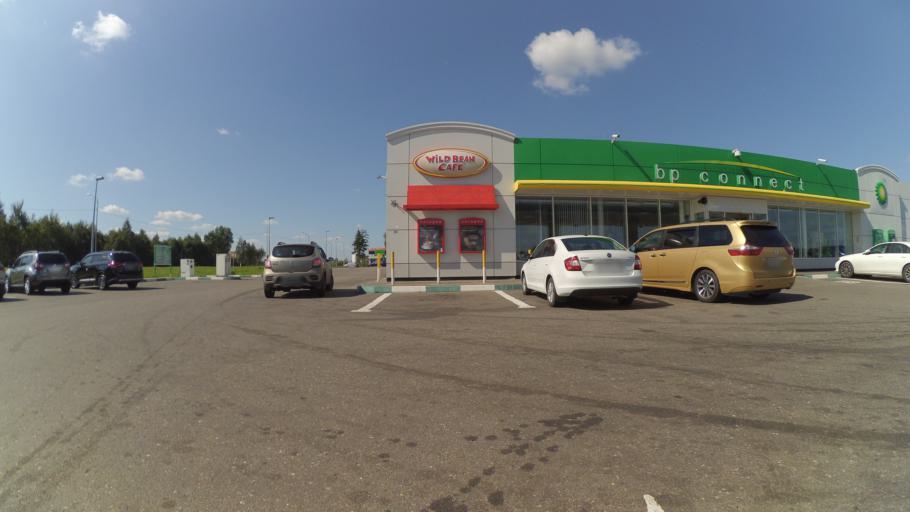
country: RU
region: Smolensk
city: Rudnya
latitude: 54.6963
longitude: 31.1226
